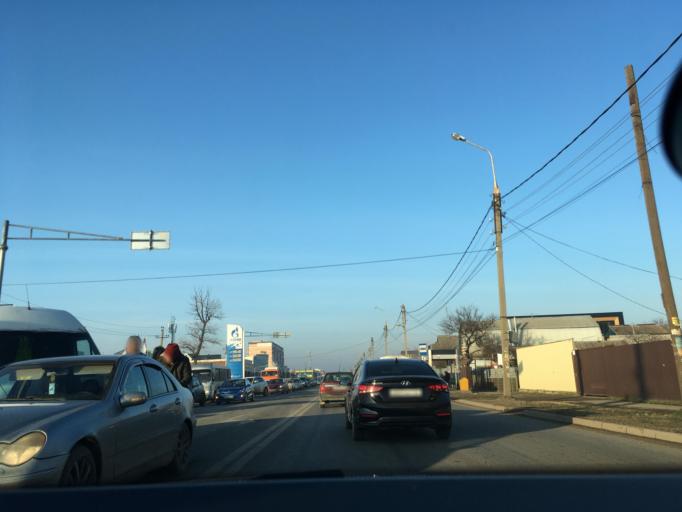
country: RU
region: Krasnodarskiy
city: Krasnodar
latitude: 45.1108
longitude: 39.0123
